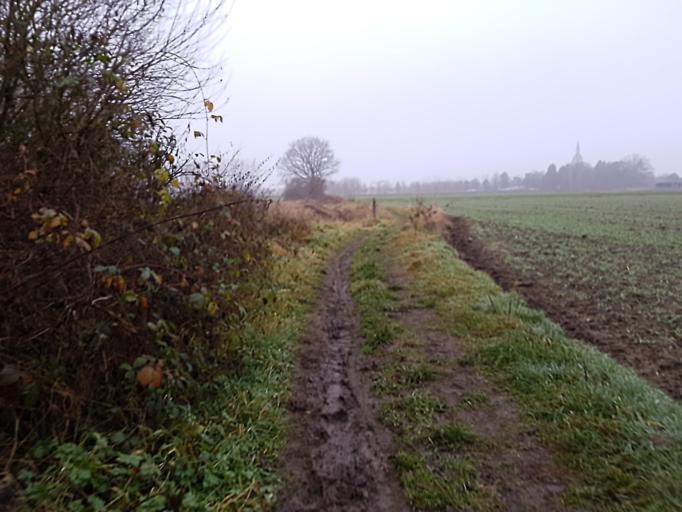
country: BE
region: Flanders
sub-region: Provincie Vlaams-Brabant
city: Boortmeerbeek
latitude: 50.9963
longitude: 4.5830
